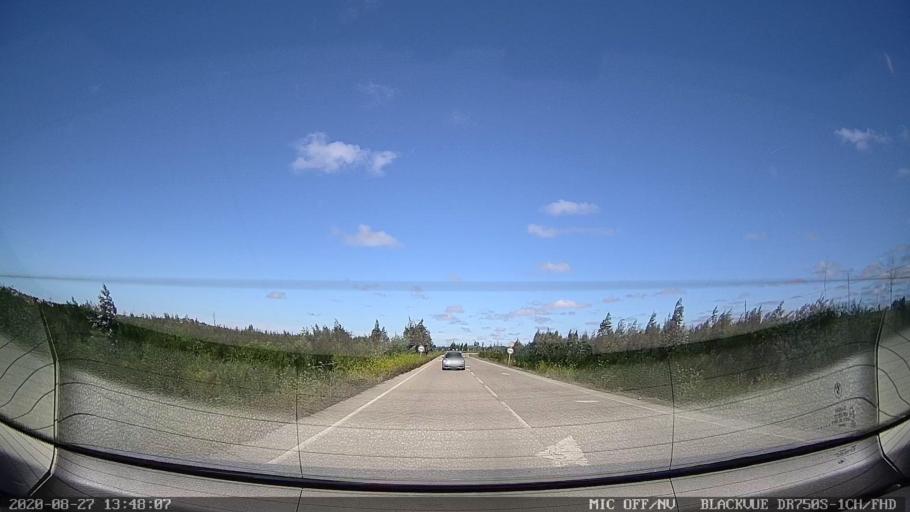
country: PT
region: Coimbra
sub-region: Mira
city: Mira
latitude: 40.3816
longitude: -8.7444
